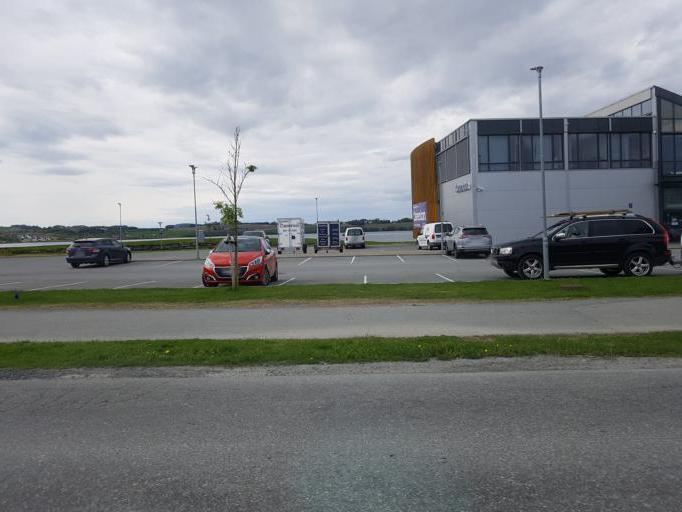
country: NO
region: Nord-Trondelag
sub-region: Levanger
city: Levanger
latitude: 63.7349
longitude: 11.2816
